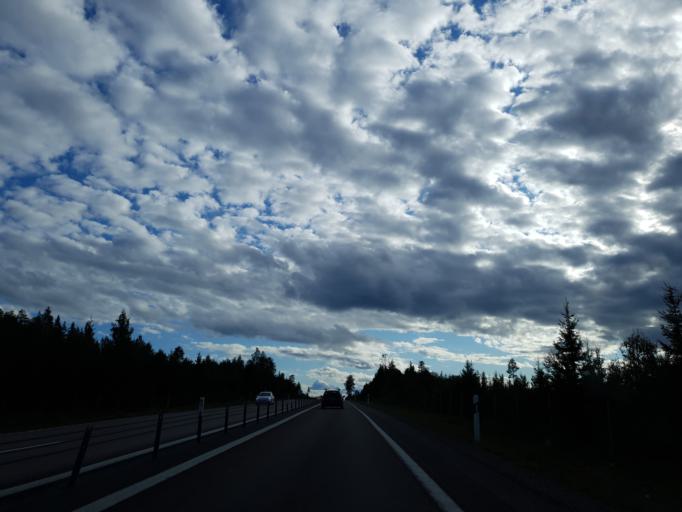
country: SE
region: Vaesternorrland
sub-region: Haernoesands Kommun
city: Haernoesand
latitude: 62.6043
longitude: 17.8179
